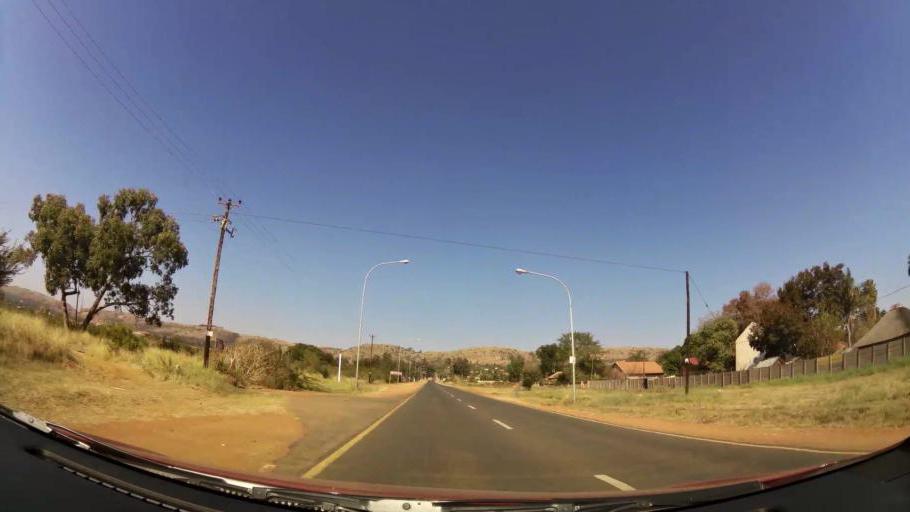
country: ZA
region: Gauteng
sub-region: City of Tshwane Metropolitan Municipality
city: Pretoria
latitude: -25.6674
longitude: 28.1010
